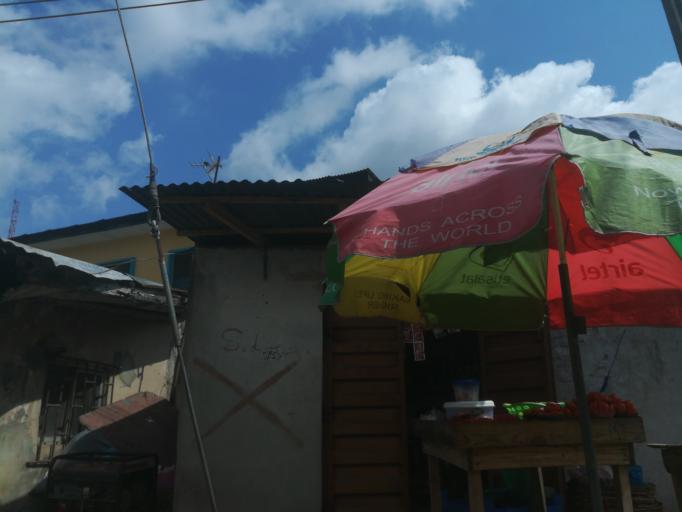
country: NG
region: Lagos
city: Somolu
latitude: 6.5302
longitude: 3.3814
